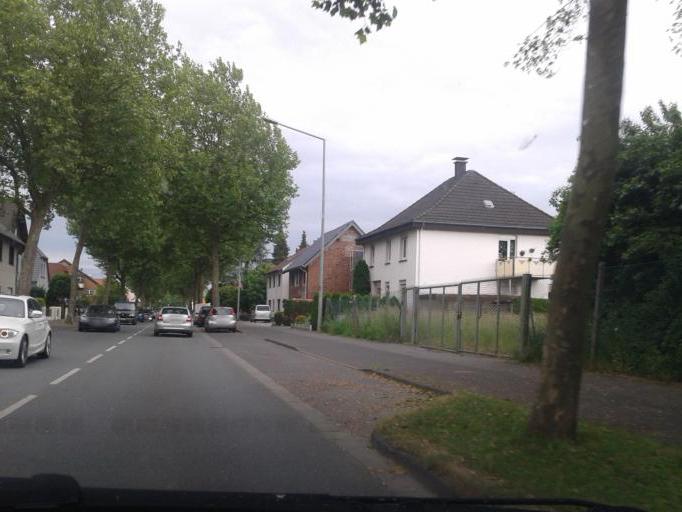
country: DE
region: North Rhine-Westphalia
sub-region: Regierungsbezirk Detmold
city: Paderborn
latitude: 51.7444
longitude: 8.7038
